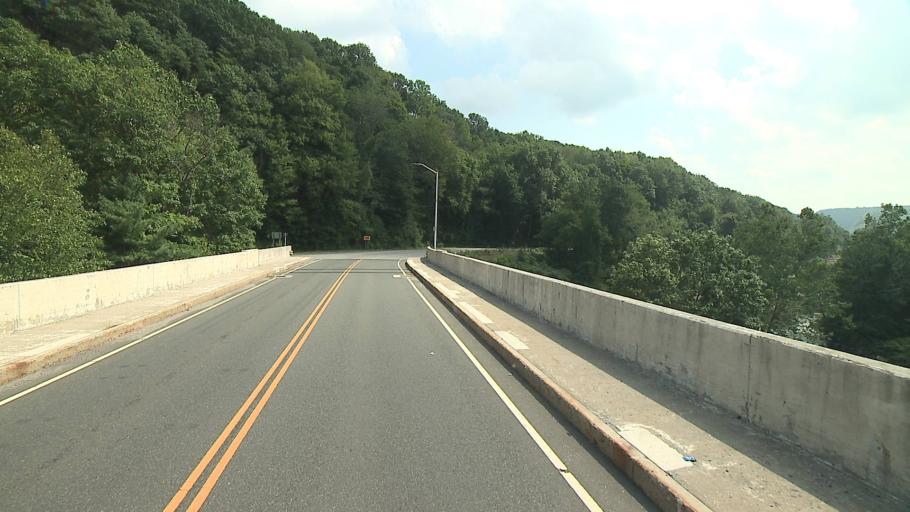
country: US
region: Connecticut
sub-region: Litchfield County
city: Thomaston
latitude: 41.6528
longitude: -73.0768
